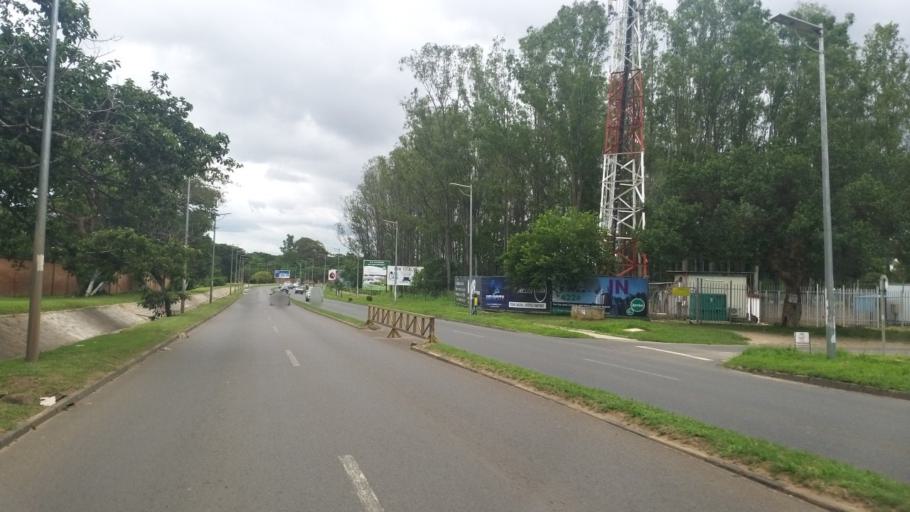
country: ZM
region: Lusaka
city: Lusaka
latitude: -15.4237
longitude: 28.3312
